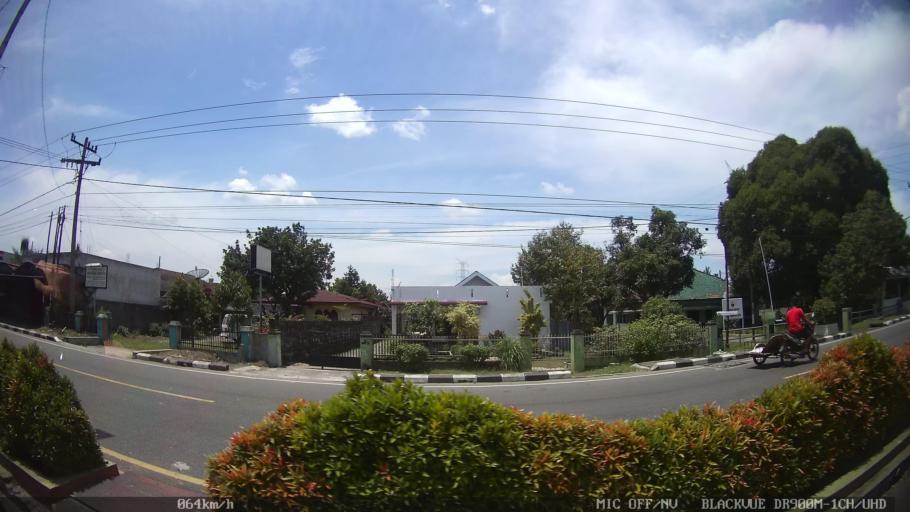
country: ID
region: North Sumatra
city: Binjai
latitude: 3.6087
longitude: 98.5090
